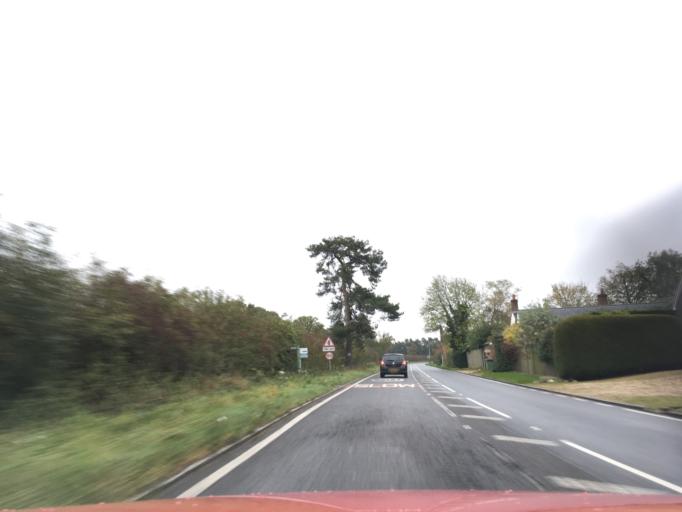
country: GB
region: England
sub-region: West Berkshire
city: Welford
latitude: 51.4264
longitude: -1.4001
